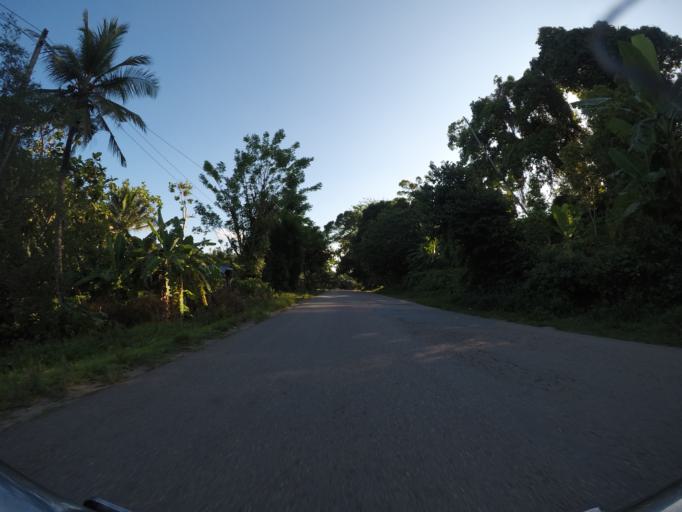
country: TZ
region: Pemba South
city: Chake Chake
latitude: -5.3151
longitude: 39.7446
